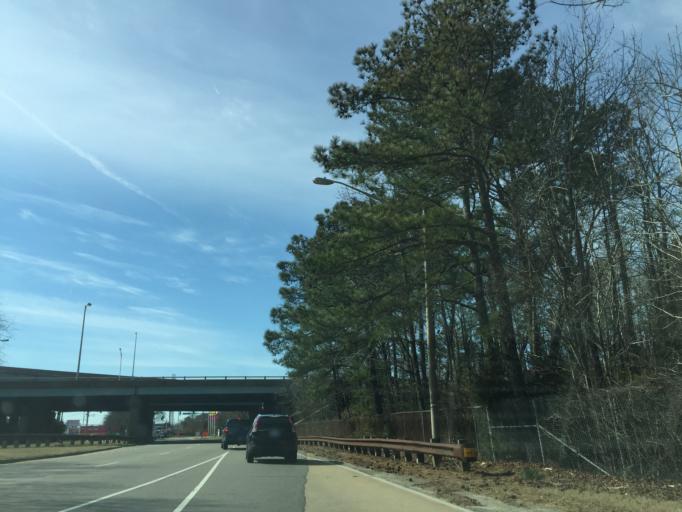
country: US
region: Virginia
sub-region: City of Norfolk
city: Norfolk
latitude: 36.9196
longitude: -76.2716
